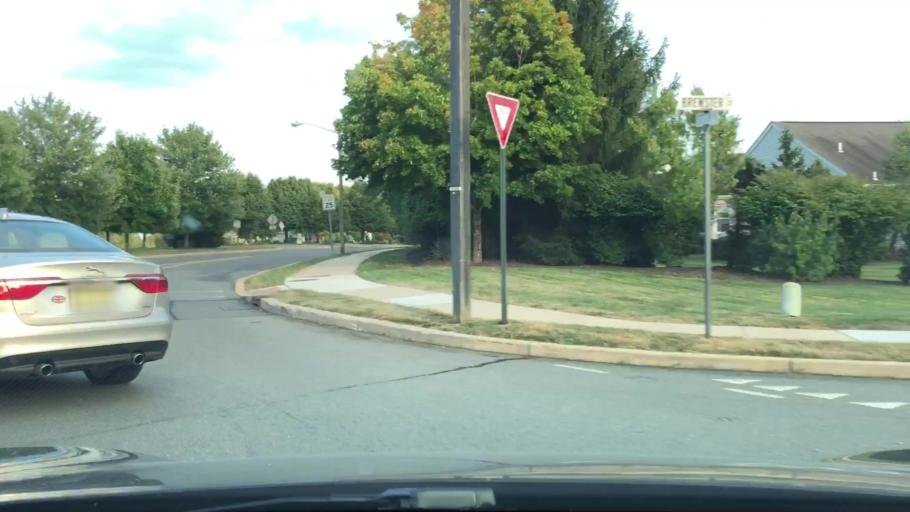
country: US
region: New Jersey
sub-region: Mercer County
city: Pennington
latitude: 40.3011
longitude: -74.7691
